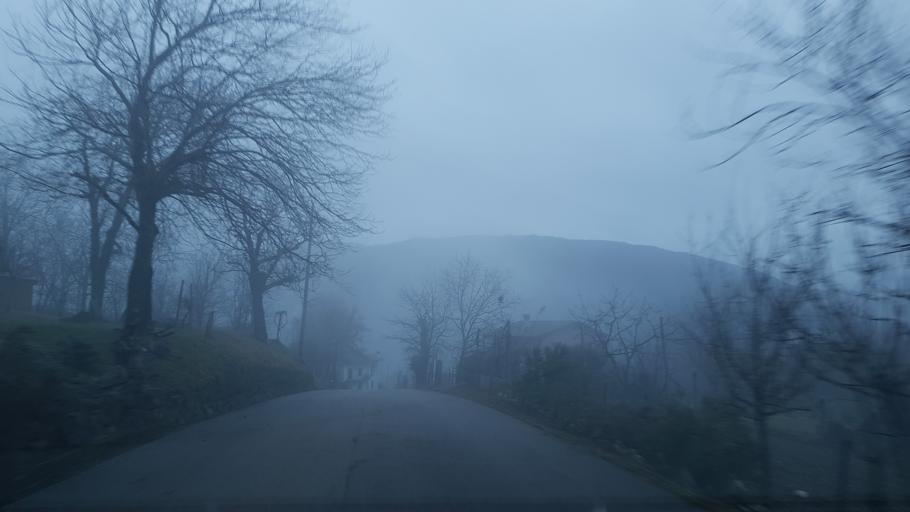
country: IT
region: Friuli Venezia Giulia
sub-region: Provincia di Udine
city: San Leonardo
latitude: 46.0910
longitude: 13.5481
